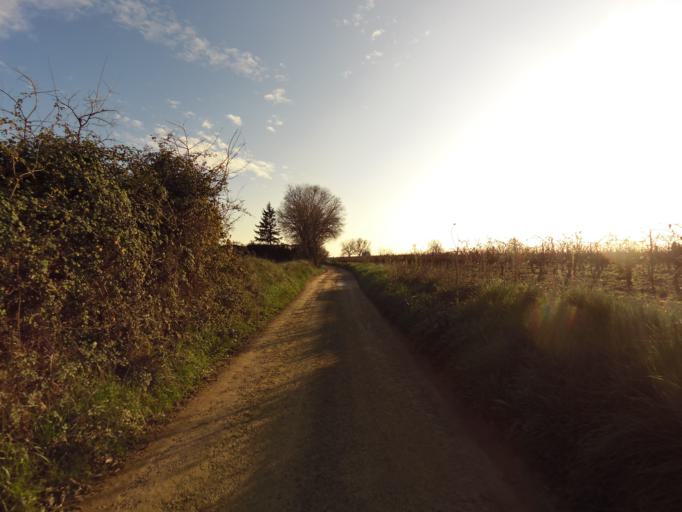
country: FR
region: Languedoc-Roussillon
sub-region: Departement du Gard
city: Gallargues-le-Montueux
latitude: 43.7167
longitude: 4.1884
